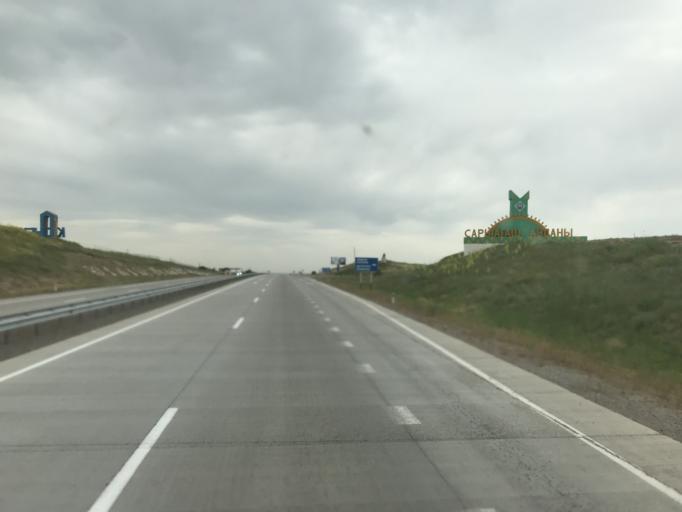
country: KZ
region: Ongtustik Qazaqstan
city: Qazyqurt
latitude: 41.6085
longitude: 69.4038
